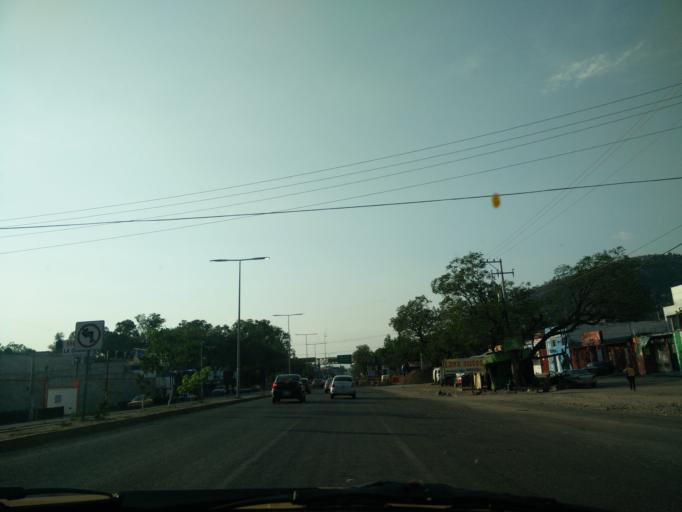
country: MX
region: Oaxaca
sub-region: Santa Maria Atzompa
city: San Jeronimo Yahuiche
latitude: 17.1000
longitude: -96.7510
